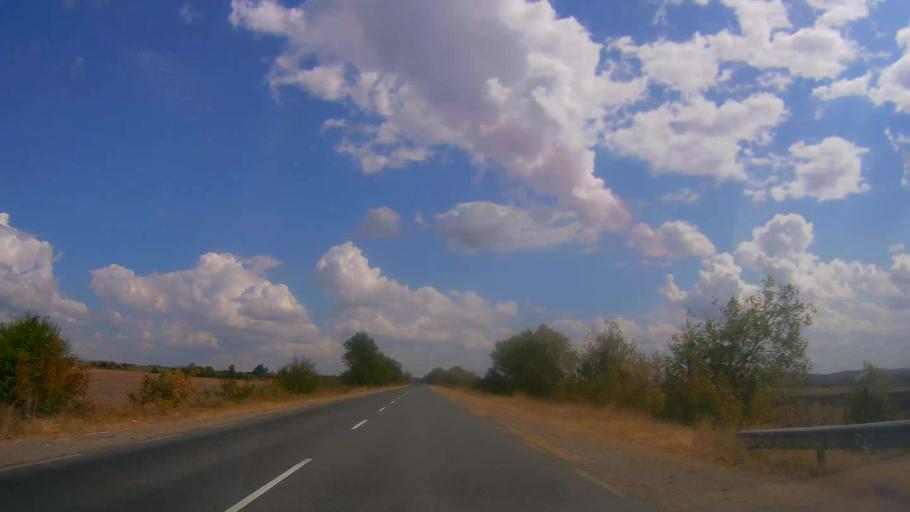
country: BG
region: Sliven
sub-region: Obshtina Sliven
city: Kermen
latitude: 42.6341
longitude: 26.1634
